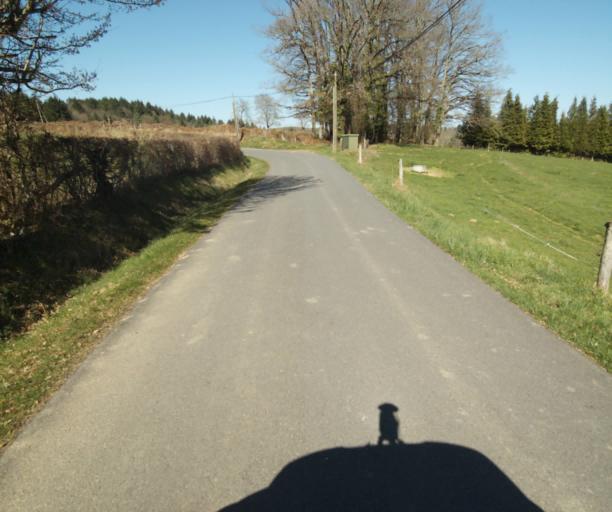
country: FR
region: Limousin
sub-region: Departement de la Correze
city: Tulle
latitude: 45.2767
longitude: 1.7261
